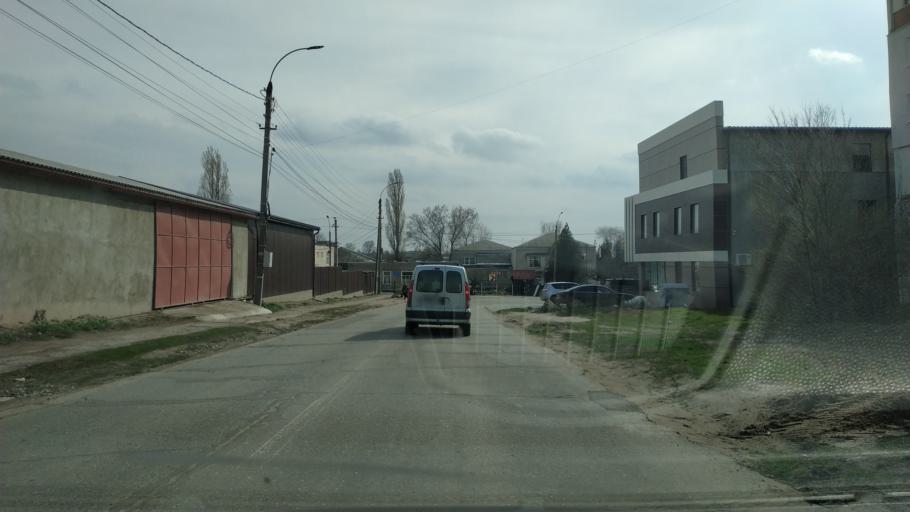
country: MD
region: Gagauzia
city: Vulcanesti
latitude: 45.6891
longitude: 28.4066
